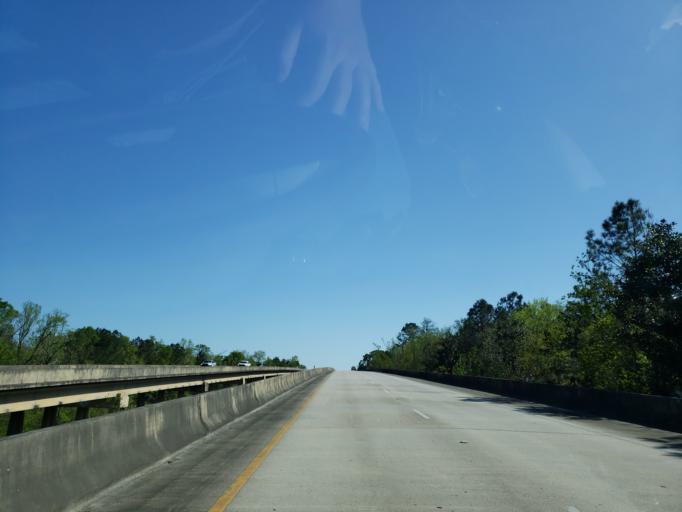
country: US
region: Mississippi
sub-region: Harrison County
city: Lyman
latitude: 30.4879
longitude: -89.0289
